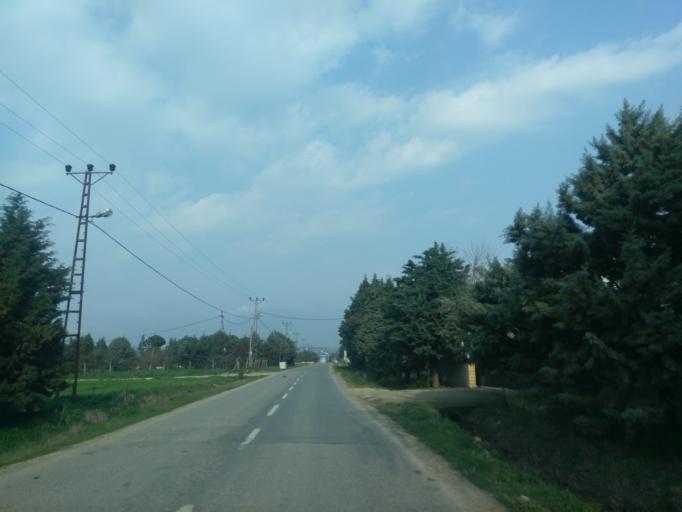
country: TR
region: Istanbul
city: Kavakli
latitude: 41.1129
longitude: 28.3018
